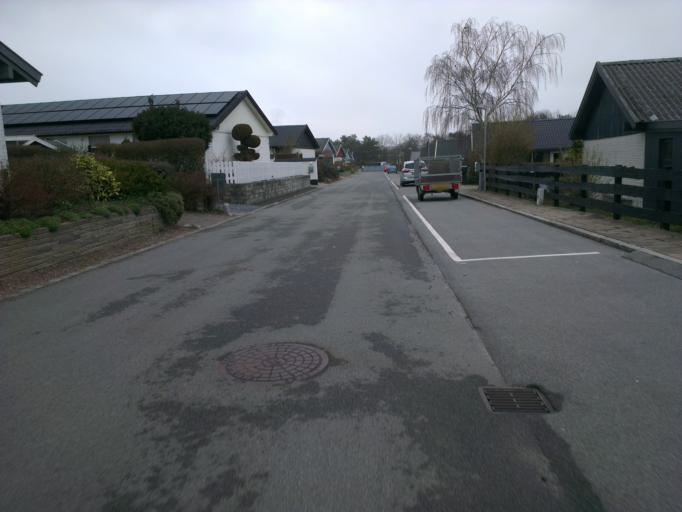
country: DK
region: Capital Region
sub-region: Frederikssund Kommune
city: Frederikssund
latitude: 55.8484
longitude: 12.0515
